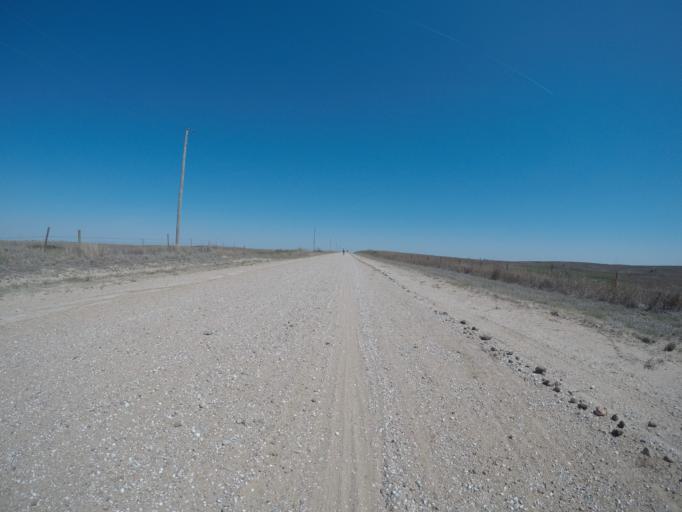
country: US
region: Kansas
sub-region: Pratt County
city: Pratt
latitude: 37.4097
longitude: -98.8401
